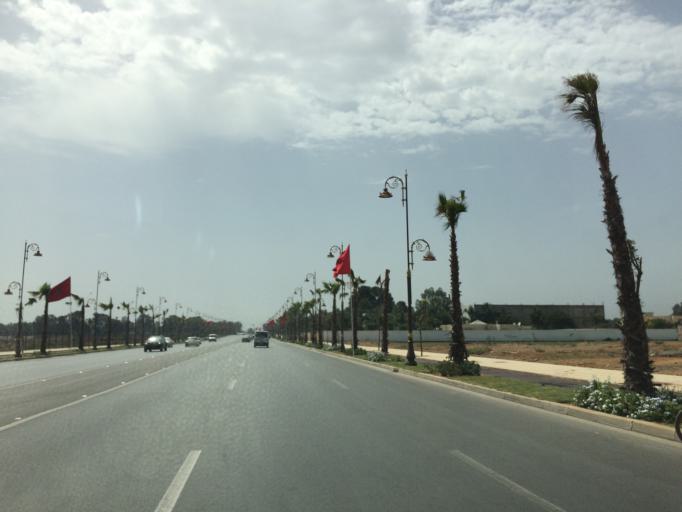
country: MA
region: Rabat-Sale-Zemmour-Zaer
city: Sale
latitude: 34.0325
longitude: -6.7691
